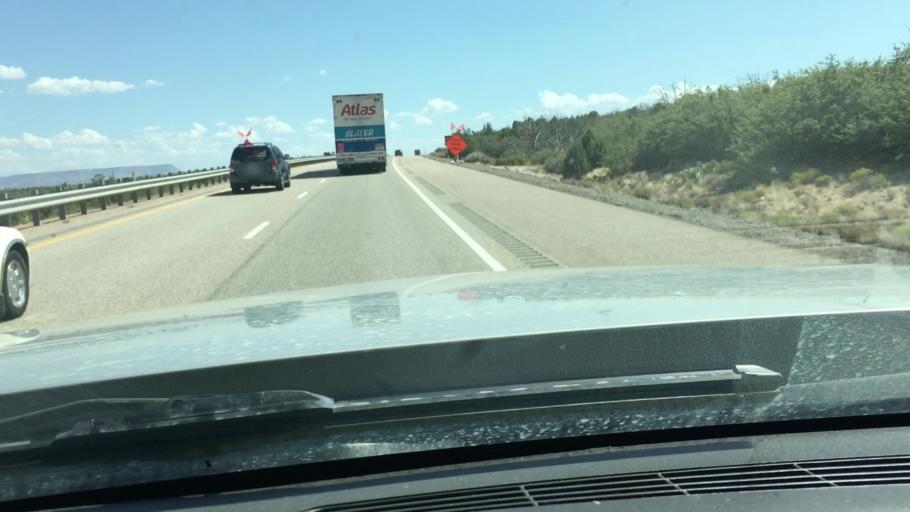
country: US
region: Utah
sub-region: Washington County
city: Toquerville
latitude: 37.2982
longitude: -113.2998
